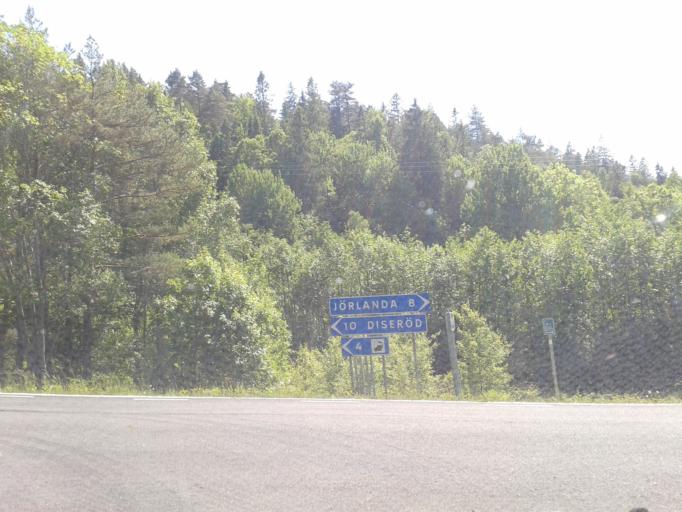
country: SE
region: Vaestra Goetaland
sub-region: Kungalvs Kommun
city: Diserod
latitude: 57.9760
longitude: 11.9561
